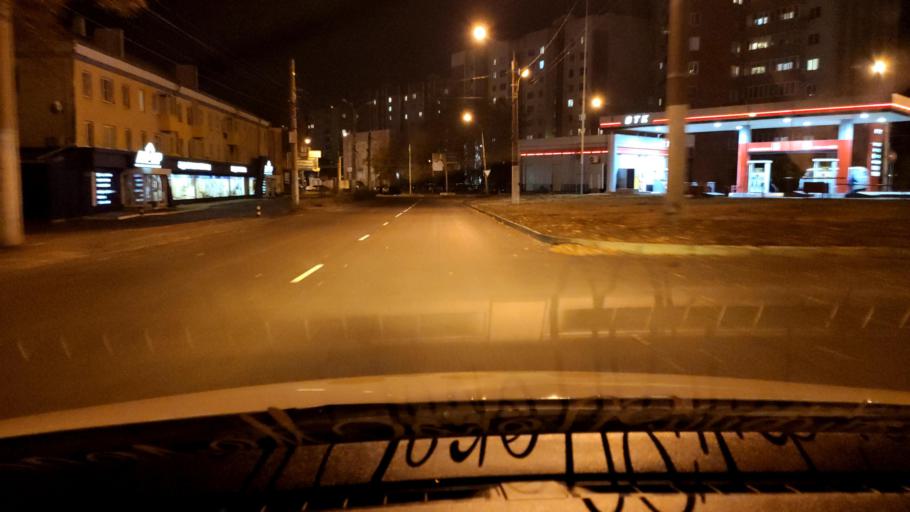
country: RU
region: Voronezj
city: Voronezh
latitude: 51.6635
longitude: 39.1572
